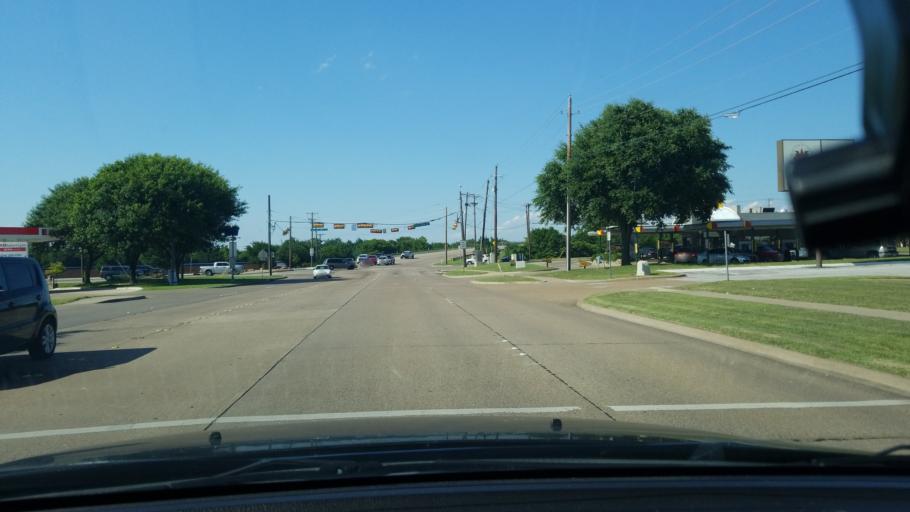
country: US
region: Texas
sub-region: Dallas County
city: Mesquite
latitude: 32.7631
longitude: -96.5824
